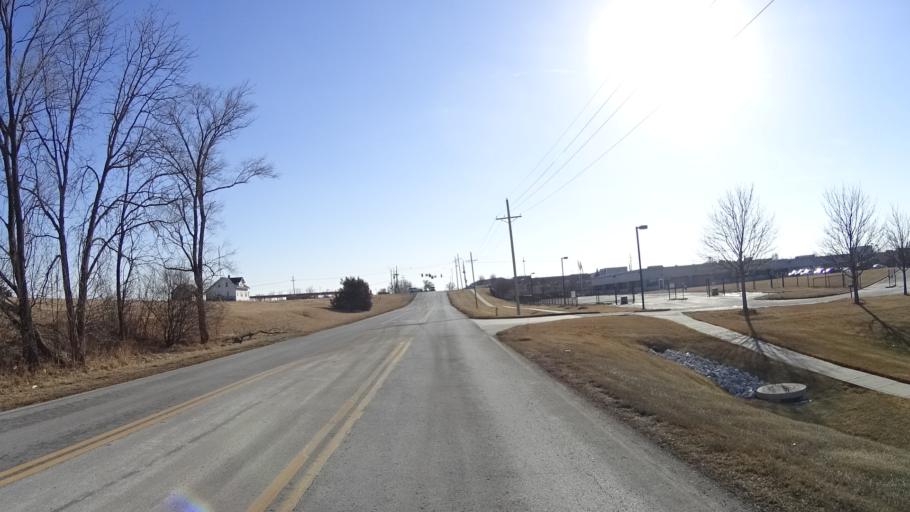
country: US
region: Nebraska
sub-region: Douglas County
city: Bennington
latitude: 41.3086
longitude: -96.1197
